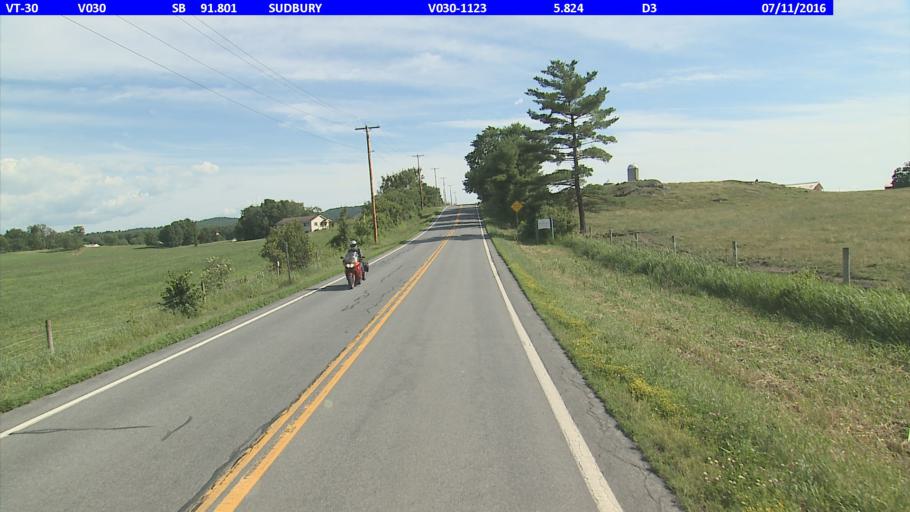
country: US
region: Vermont
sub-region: Rutland County
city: Brandon
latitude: 43.8300
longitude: -73.1935
